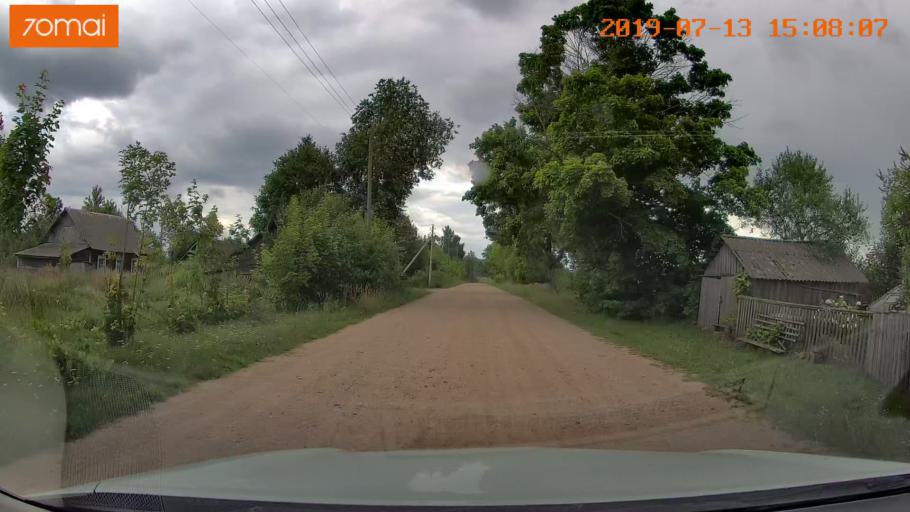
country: BY
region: Mogilev
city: Hlusha
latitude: 53.1821
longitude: 28.7574
